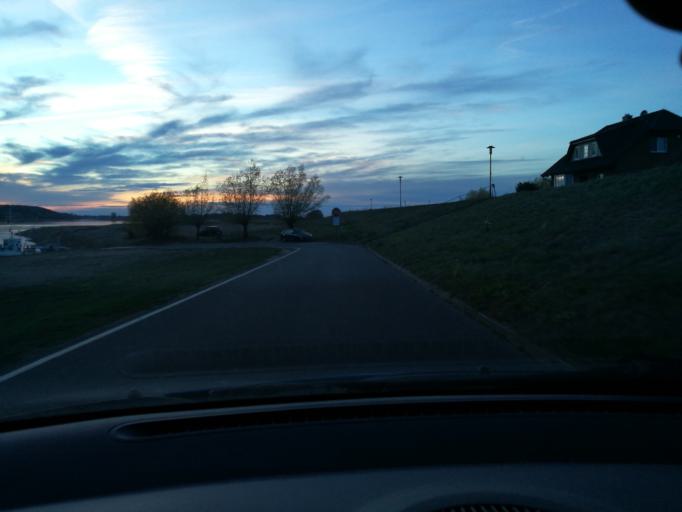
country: DE
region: Brandenburg
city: Lenzen
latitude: 53.0803
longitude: 11.4536
